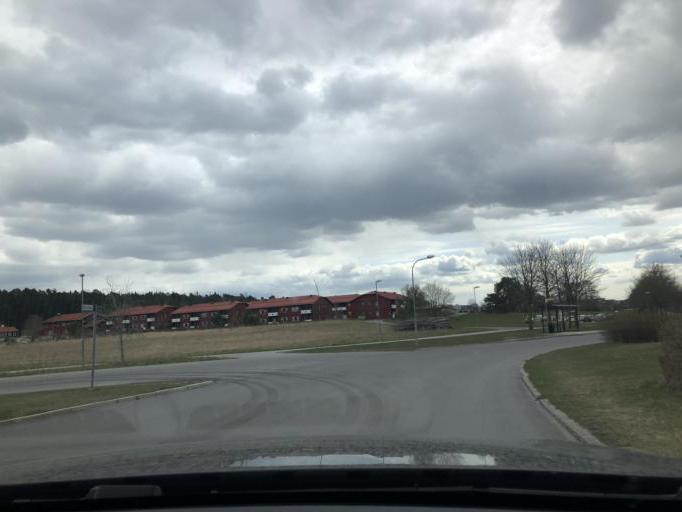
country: SE
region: Uppsala
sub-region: Uppsala Kommun
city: Uppsala
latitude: 59.8229
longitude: 17.6561
